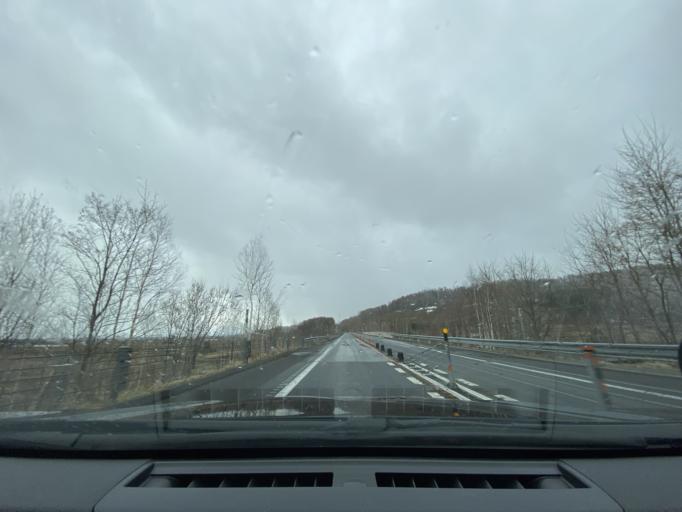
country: JP
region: Hokkaido
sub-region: Asahikawa-shi
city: Asahikawa
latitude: 43.9055
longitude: 142.4663
